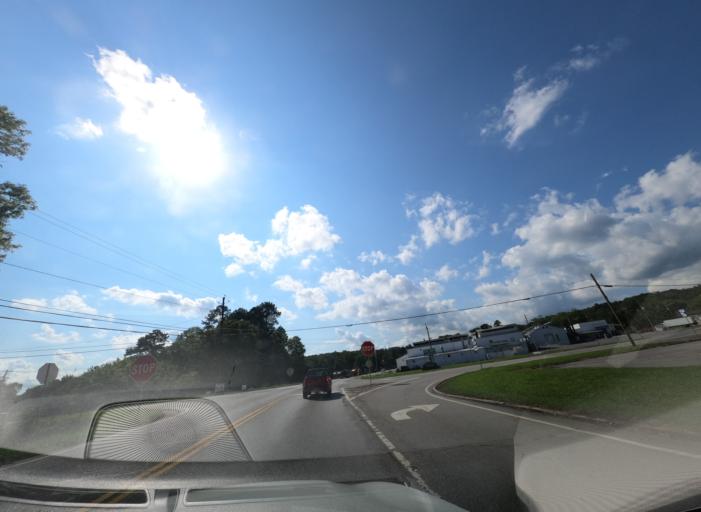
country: US
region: Georgia
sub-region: Chattooga County
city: Summerville
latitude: 34.4830
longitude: -85.4763
